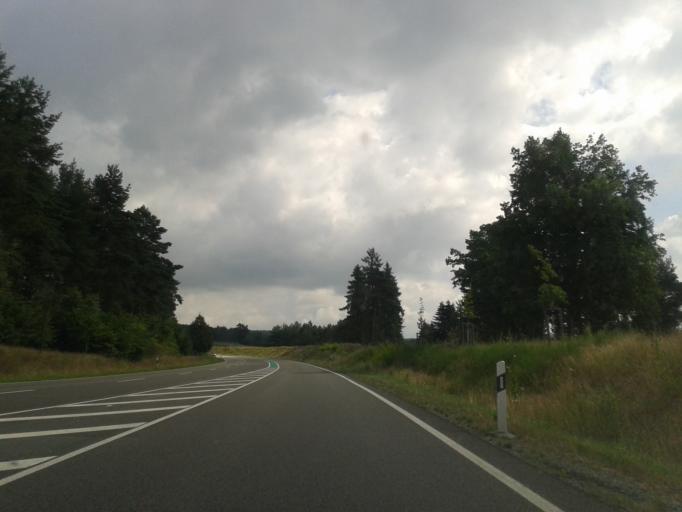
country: DE
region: Saxony
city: Pirna
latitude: 50.9887
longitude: 13.9321
